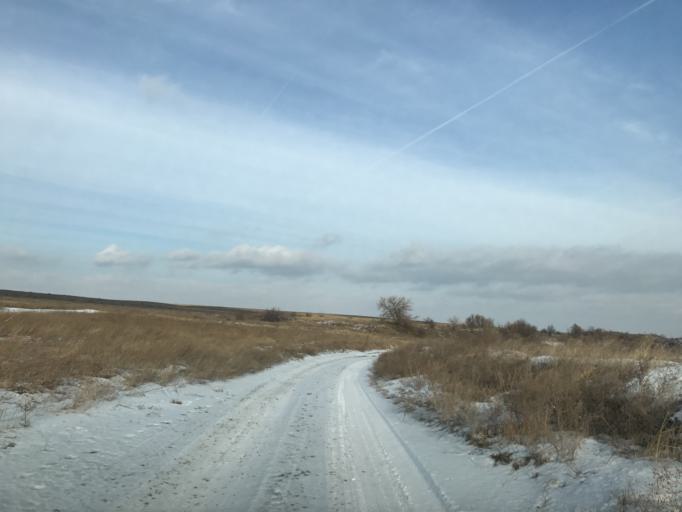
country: RU
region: Rostov
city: Staraya Stanitsa
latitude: 48.2458
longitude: 40.3992
